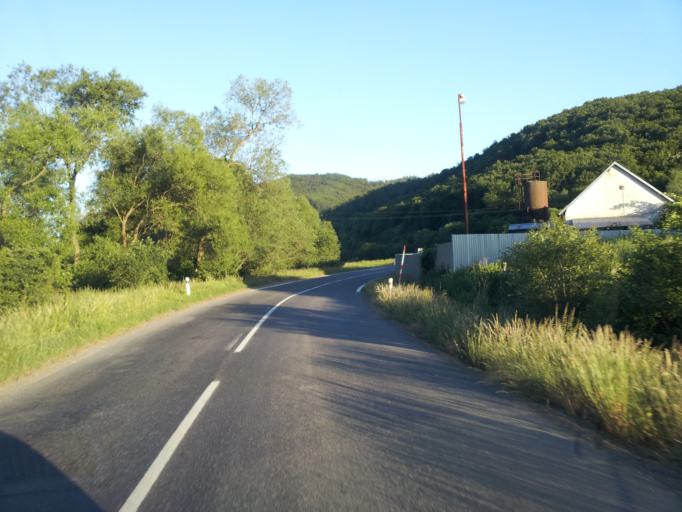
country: SK
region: Banskobystricky
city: Svaety Anton
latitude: 48.3490
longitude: 18.9300
